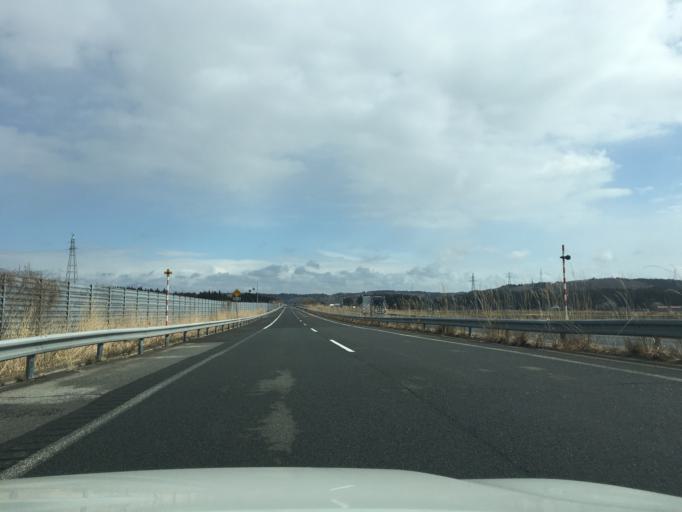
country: JP
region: Akita
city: Akita
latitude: 39.6150
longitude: 140.1436
